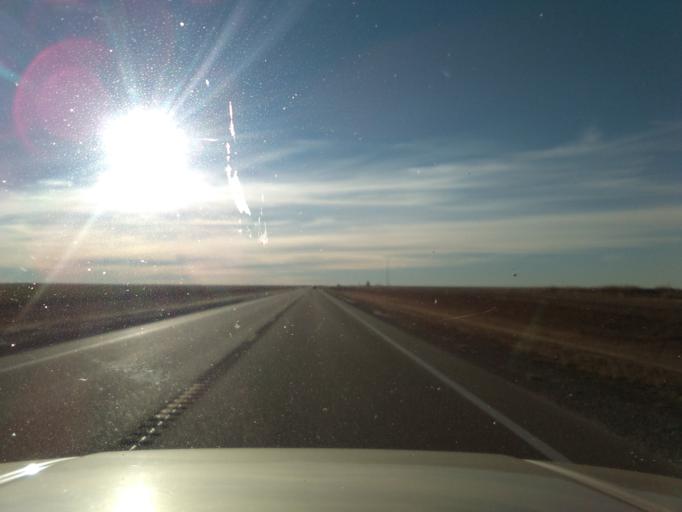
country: US
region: Kansas
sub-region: Sheridan County
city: Hoxie
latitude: 39.4884
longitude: -100.6964
